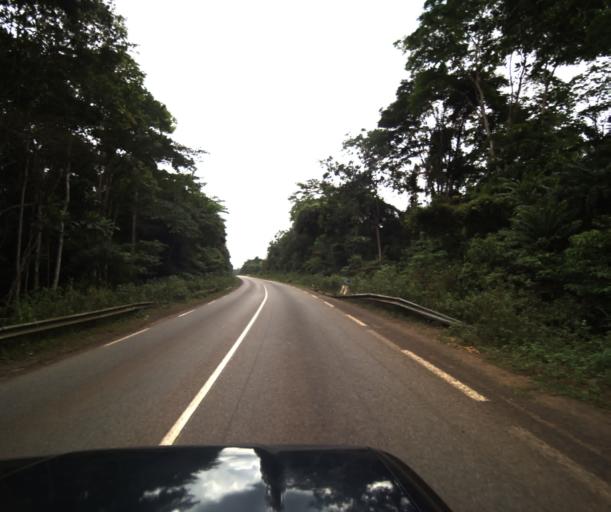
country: CM
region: Littoral
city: Edea
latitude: 3.8228
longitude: 10.3803
